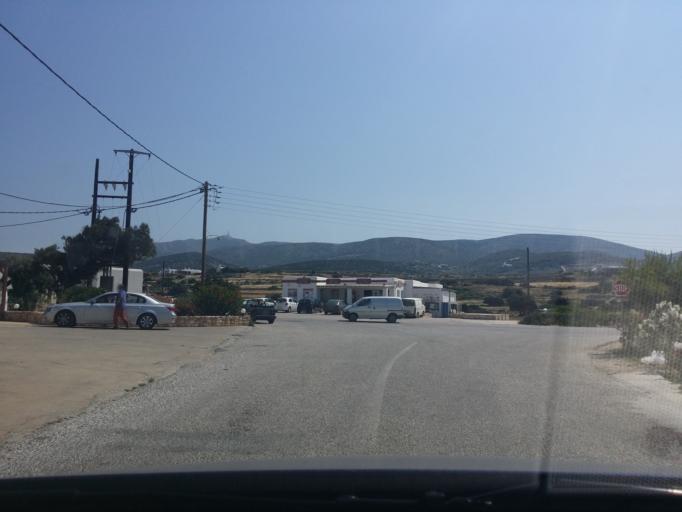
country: GR
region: South Aegean
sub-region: Nomos Kykladon
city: Antiparos
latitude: 37.0031
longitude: 25.1310
